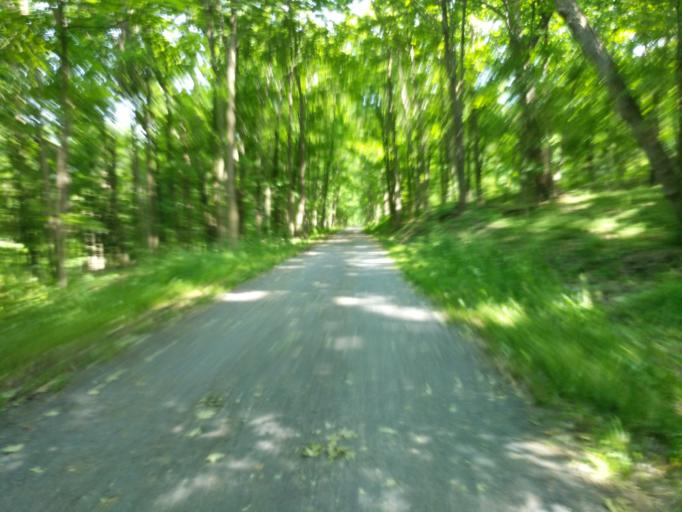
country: US
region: New York
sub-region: Tompkins County
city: Northwest Ithaca
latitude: 42.5038
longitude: -76.5490
